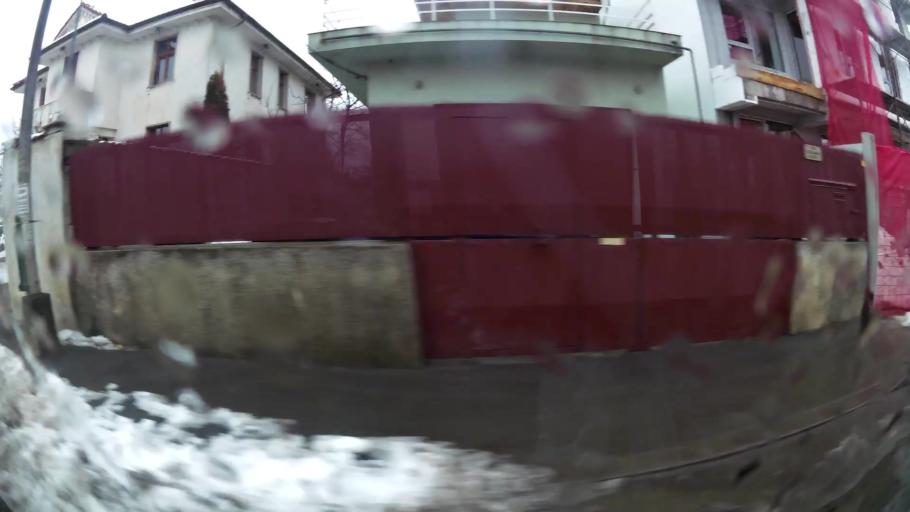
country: RO
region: Ilfov
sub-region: Comuna Chiajna
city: Rosu
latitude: 44.4097
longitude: 26.0106
